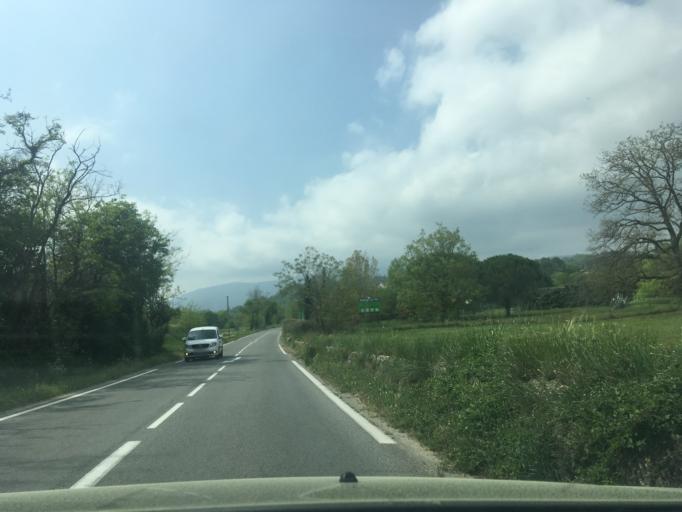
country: FR
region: Provence-Alpes-Cote d'Azur
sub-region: Departement du Var
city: Fayence
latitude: 43.6162
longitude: 6.7165
